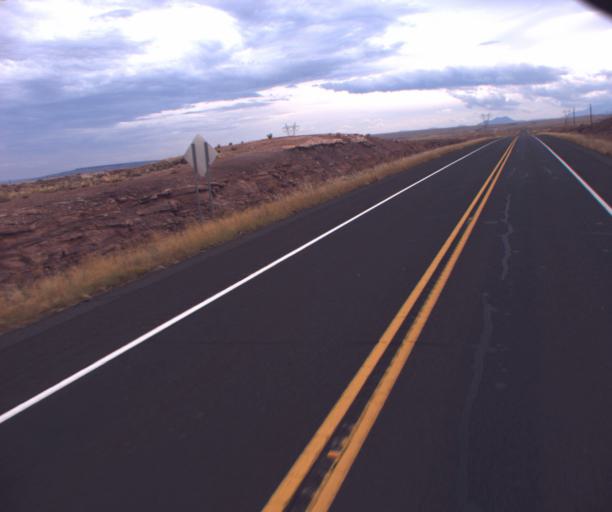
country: US
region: Arizona
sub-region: Coconino County
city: Tuba City
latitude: 35.8309
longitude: -111.4382
